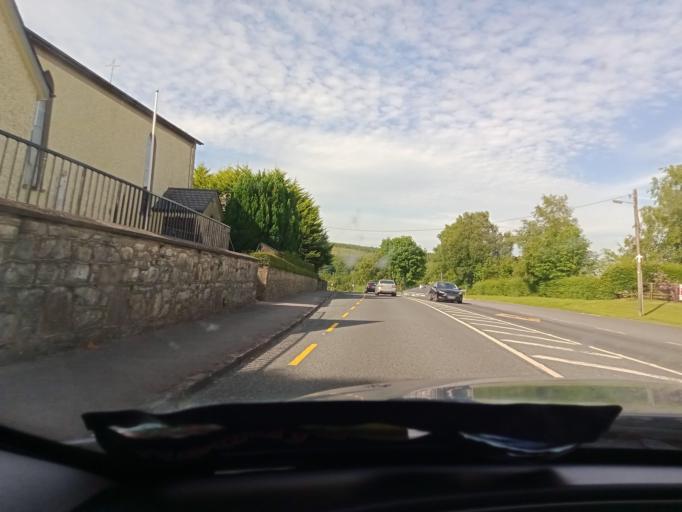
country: IE
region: Leinster
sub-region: An Iarmhi
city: An Muileann gCearr
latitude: 53.5880
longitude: -7.3030
